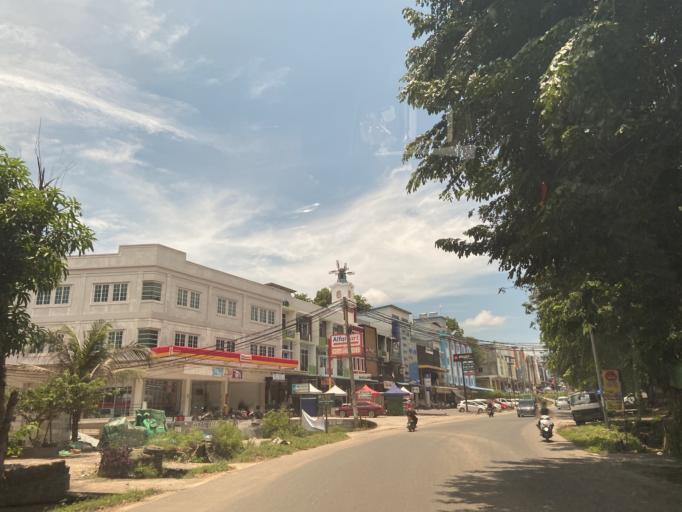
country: SG
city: Singapore
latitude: 1.1579
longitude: 104.0251
